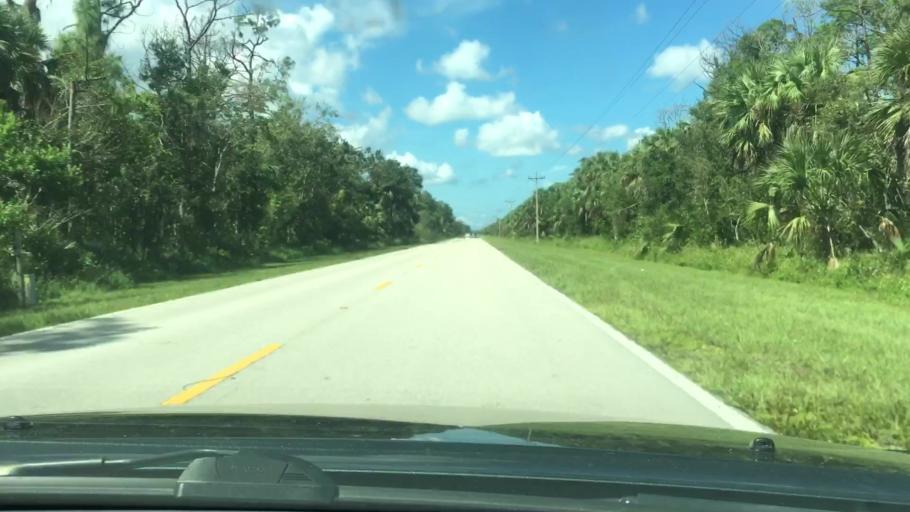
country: US
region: Florida
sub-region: Collier County
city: Lely Resort
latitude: 25.9936
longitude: -81.5949
